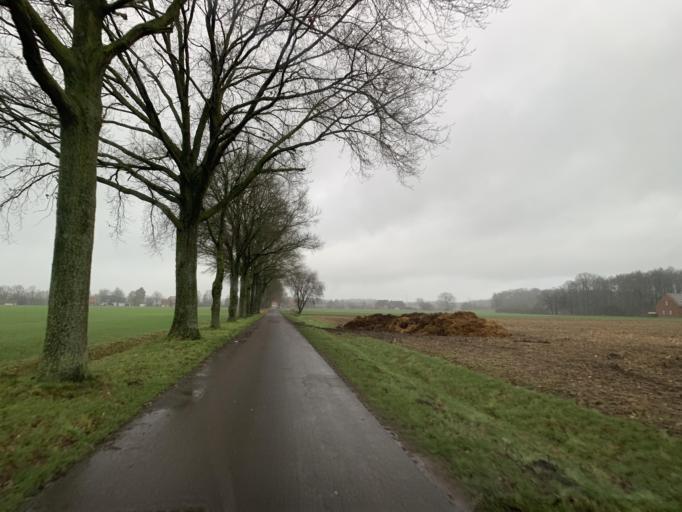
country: DE
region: North Rhine-Westphalia
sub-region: Regierungsbezirk Munster
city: Senden
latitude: 51.8968
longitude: 7.5323
